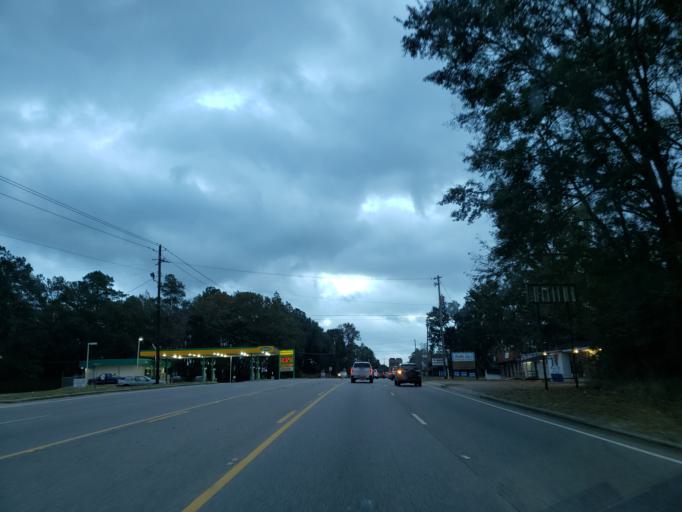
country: US
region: Alabama
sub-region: Mobile County
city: Prichard
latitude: 30.7775
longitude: -88.2493
